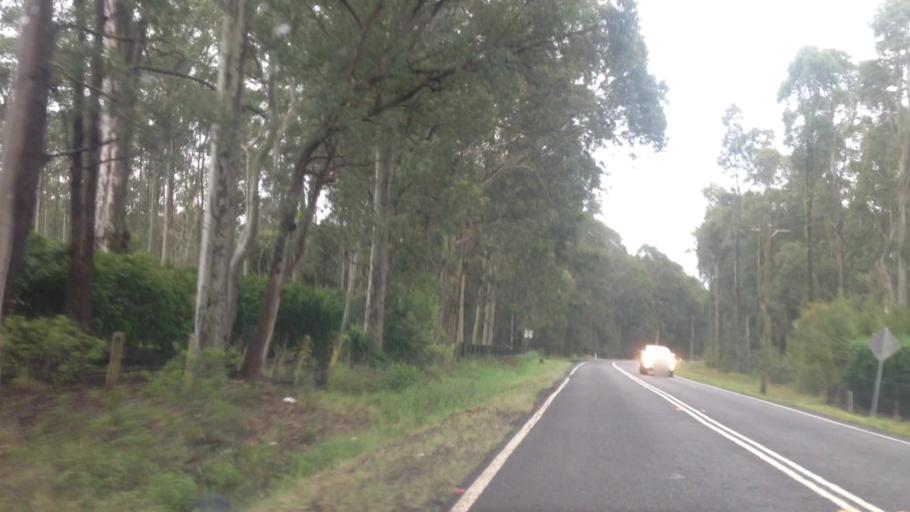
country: AU
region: New South Wales
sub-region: Wyong Shire
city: Little Jilliby
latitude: -33.2544
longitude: 151.3972
